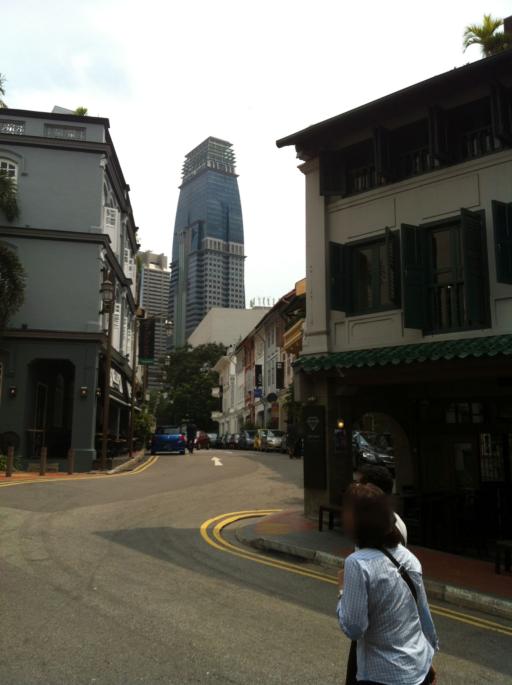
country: SG
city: Singapore
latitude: 1.2807
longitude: 103.8468
